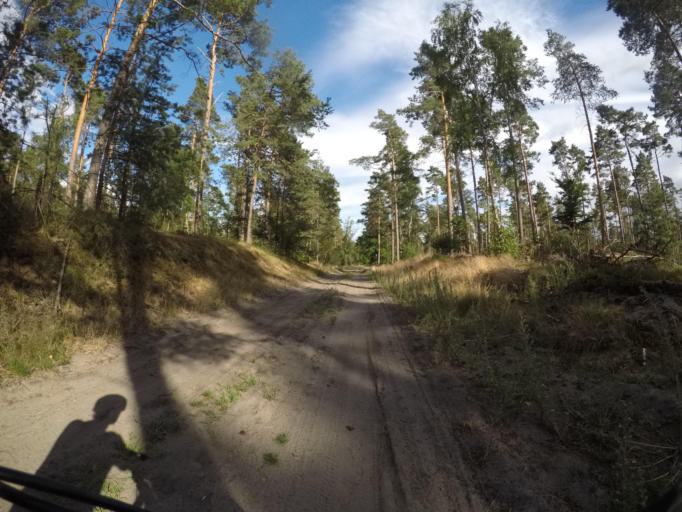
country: DE
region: Lower Saxony
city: Neu Darchau
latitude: 53.2773
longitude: 10.9521
